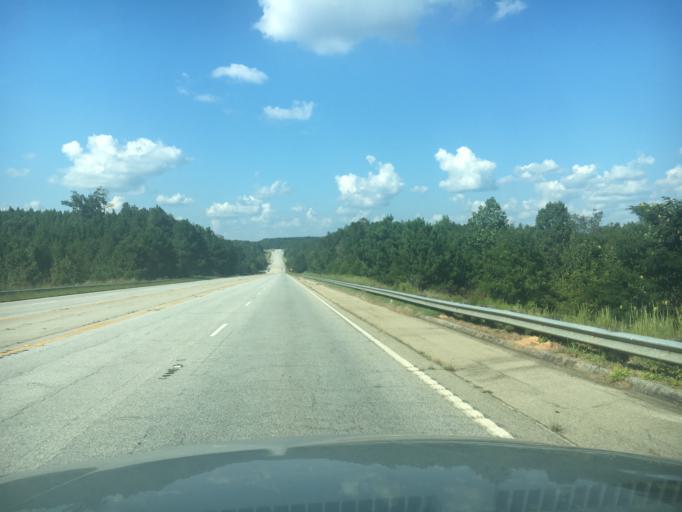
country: US
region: South Carolina
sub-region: Greenwood County
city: Ware Shoals
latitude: 34.3841
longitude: -82.2242
